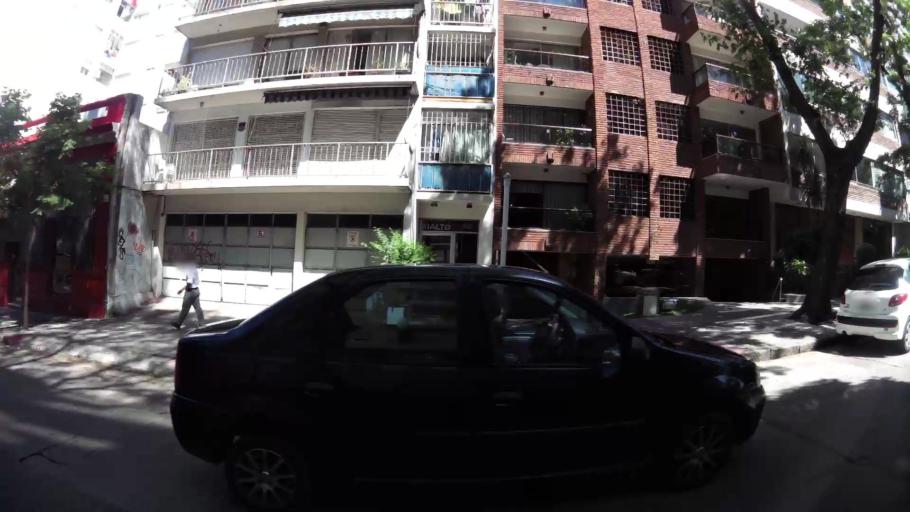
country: UY
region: Montevideo
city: Montevideo
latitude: -34.9094
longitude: -56.1488
